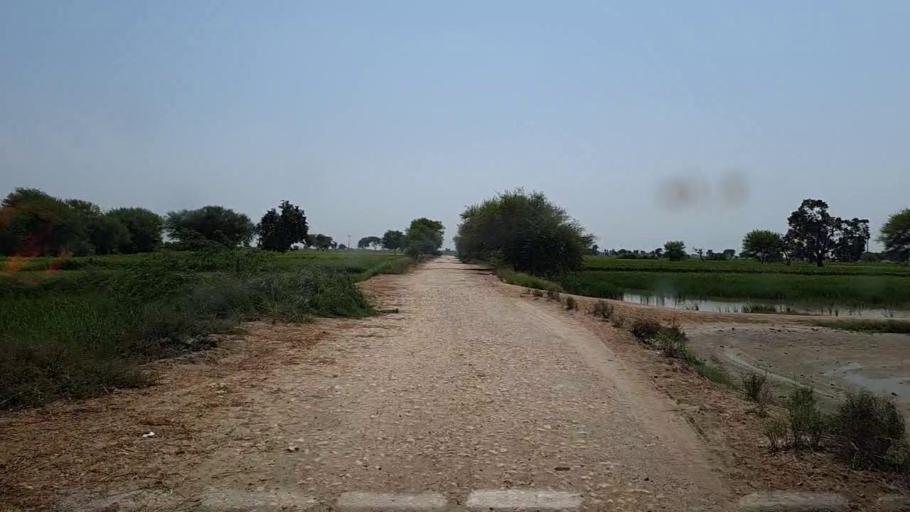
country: PK
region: Sindh
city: Kario
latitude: 24.6419
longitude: 68.4860
